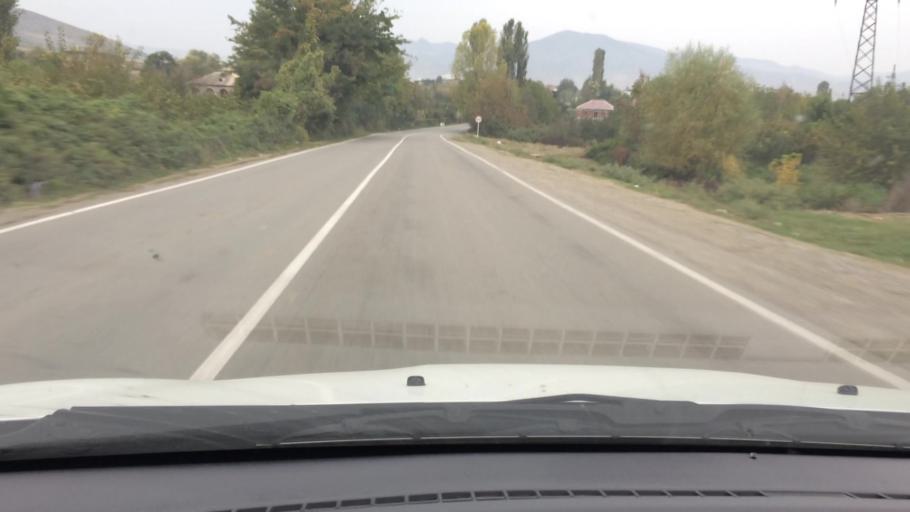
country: AM
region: Tavush
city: Bagratashen
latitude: 41.2338
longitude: 44.8131
